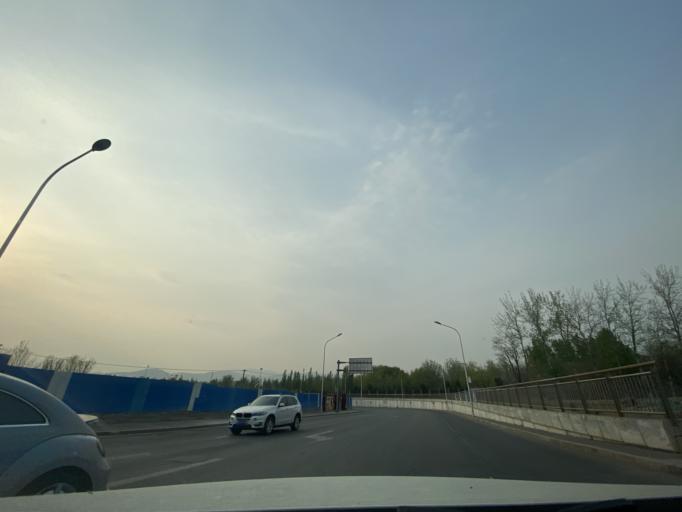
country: CN
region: Beijing
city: Babaoshan
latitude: 39.9316
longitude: 116.2225
